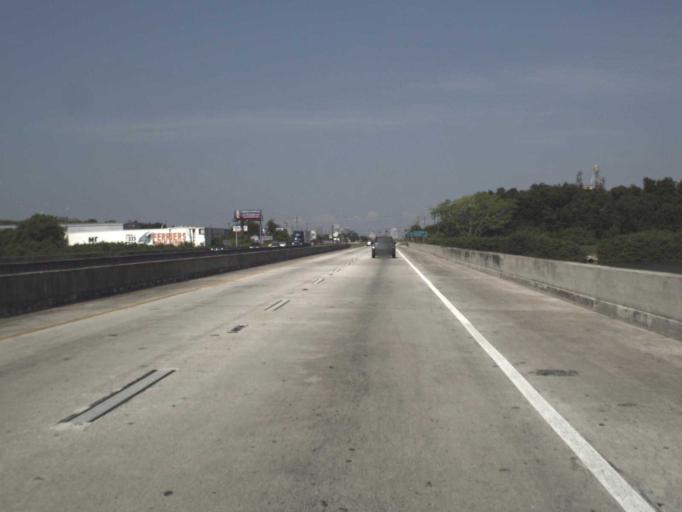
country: US
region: Florida
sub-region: Hillsborough County
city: Palm River-Clair Mel
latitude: 27.9524
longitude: -82.3699
